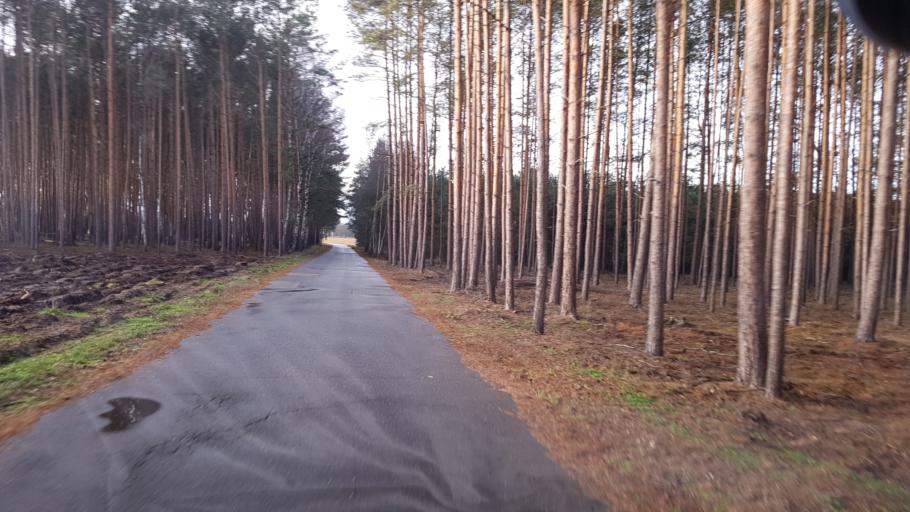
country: DE
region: Brandenburg
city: Bronkow
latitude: 51.6662
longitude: 13.8756
